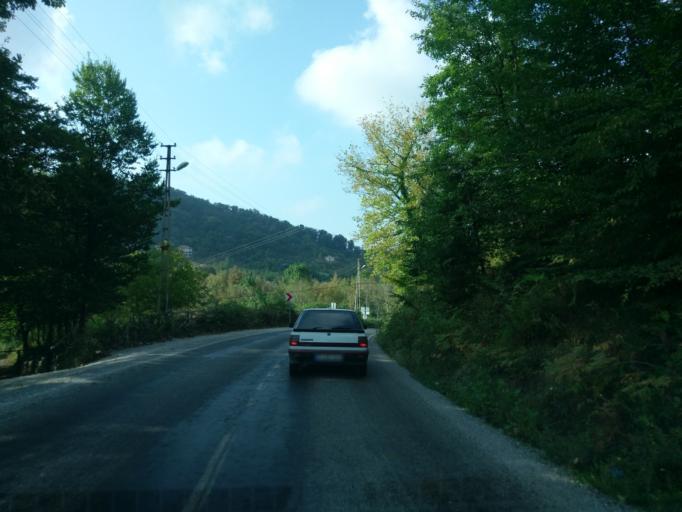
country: TR
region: Sinop
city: Helaldi
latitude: 41.9207
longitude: 34.4139
